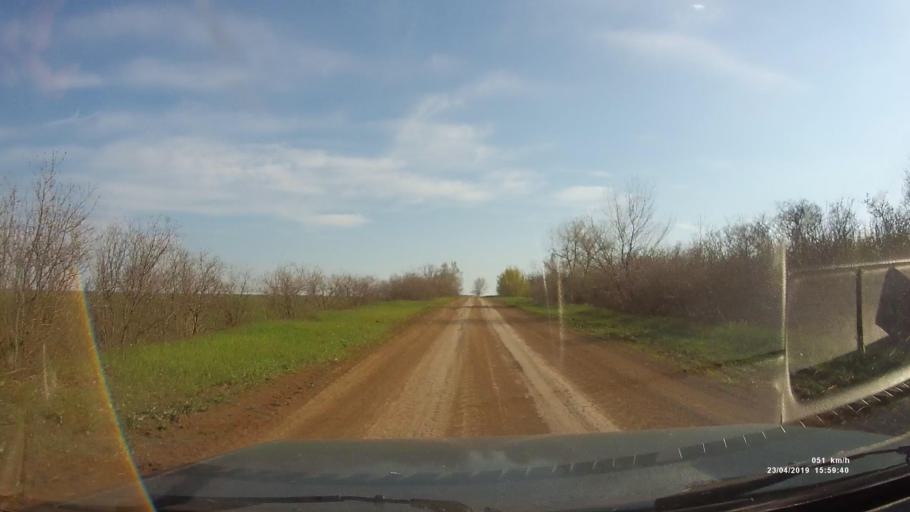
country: RU
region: Rostov
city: Remontnoye
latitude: 46.5151
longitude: 43.1096
